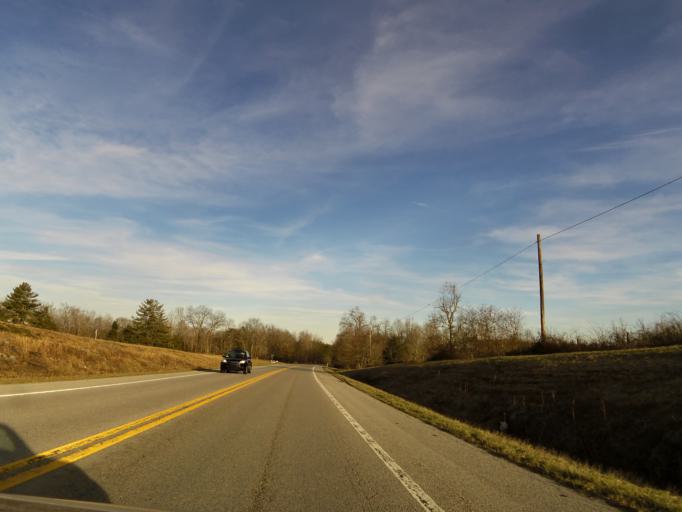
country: US
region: Tennessee
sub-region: Cumberland County
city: Crossville
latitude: 35.9546
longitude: -85.1121
